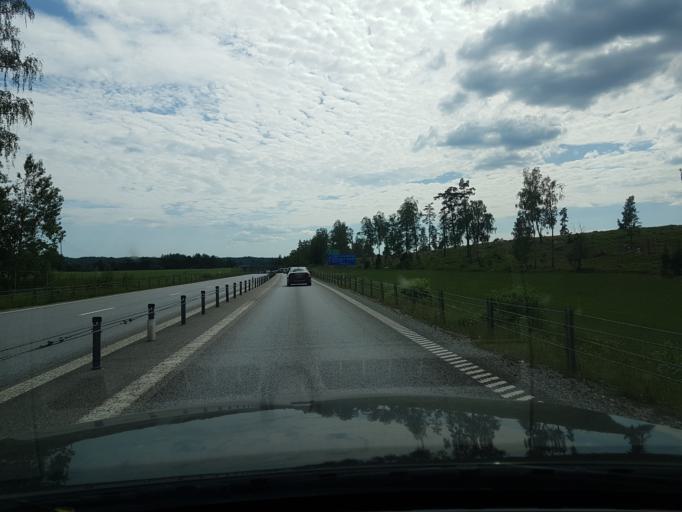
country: SE
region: Stockholm
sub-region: Osterakers Kommun
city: Akersberga
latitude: 59.5719
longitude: 18.2361
